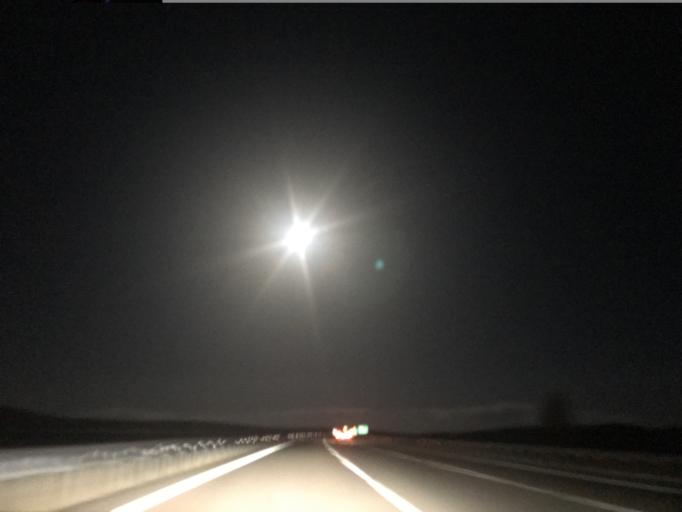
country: TR
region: Nigde
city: Ulukisla
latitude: 37.6363
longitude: 34.4979
